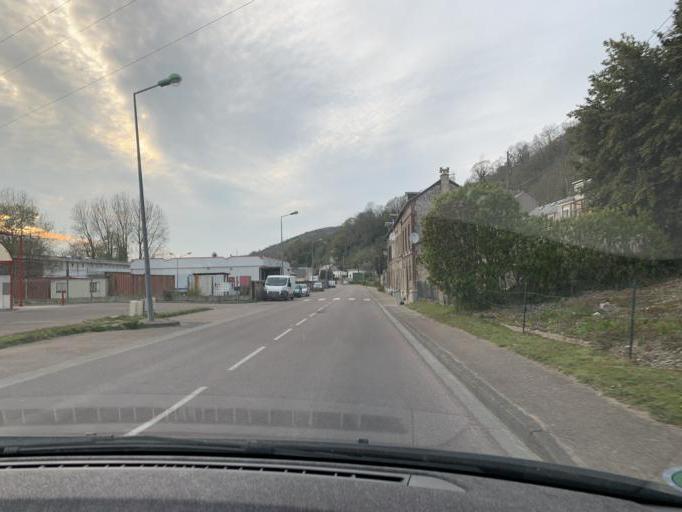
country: FR
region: Haute-Normandie
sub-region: Departement de la Seine-Maritime
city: Fecamp
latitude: 49.7553
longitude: 0.4024
